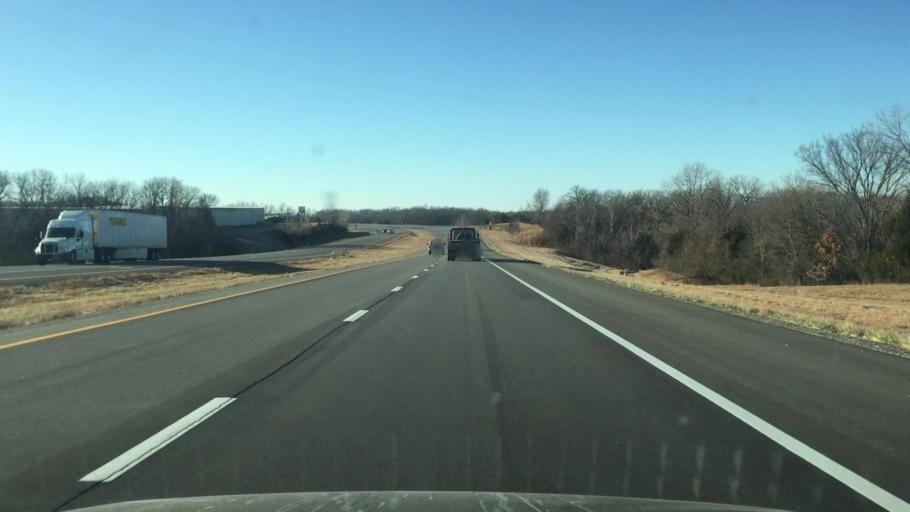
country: US
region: Kansas
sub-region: Johnson County
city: Spring Hill
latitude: 38.7569
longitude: -94.8363
